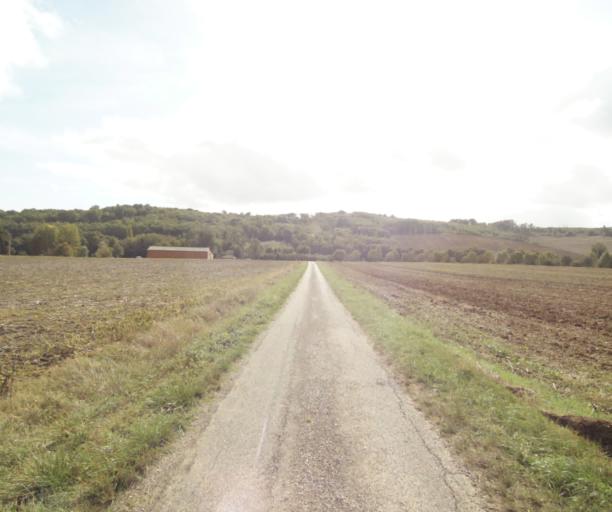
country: FR
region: Midi-Pyrenees
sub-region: Departement du Tarn-et-Garonne
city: Finhan
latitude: 43.8724
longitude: 1.1198
